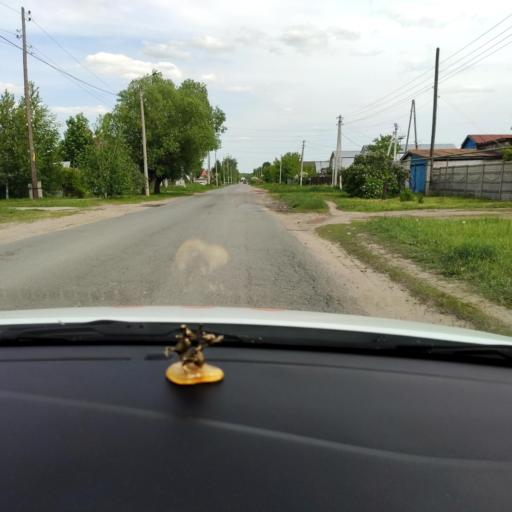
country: RU
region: Tatarstan
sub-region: Gorod Kazan'
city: Kazan
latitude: 55.7013
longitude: 49.0689
